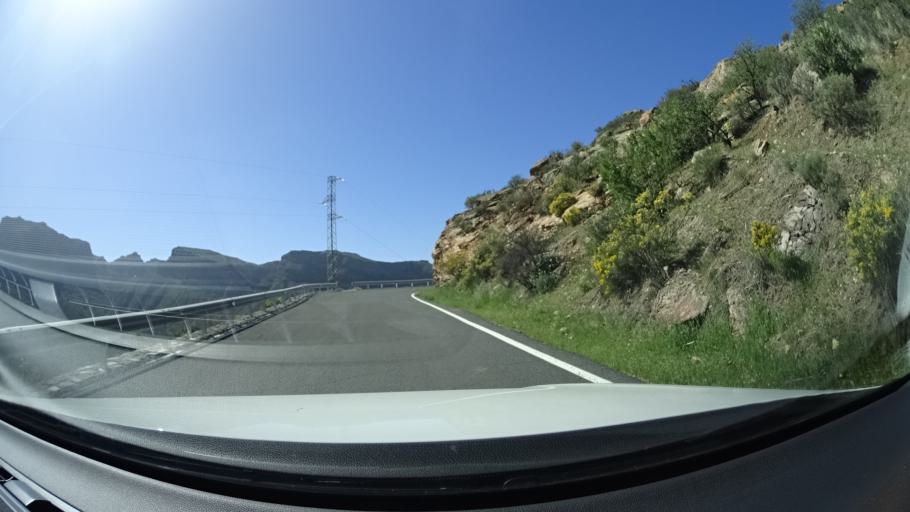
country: ES
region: Canary Islands
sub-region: Provincia de Las Palmas
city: Tejeda
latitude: 27.9874
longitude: -15.6387
